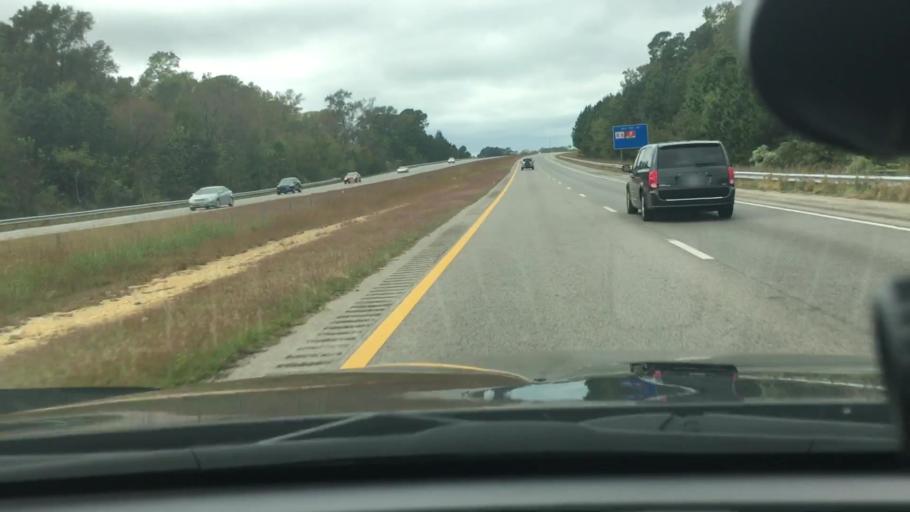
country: US
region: North Carolina
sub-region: Wilson County
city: Wilson
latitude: 35.6771
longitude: -77.9431
